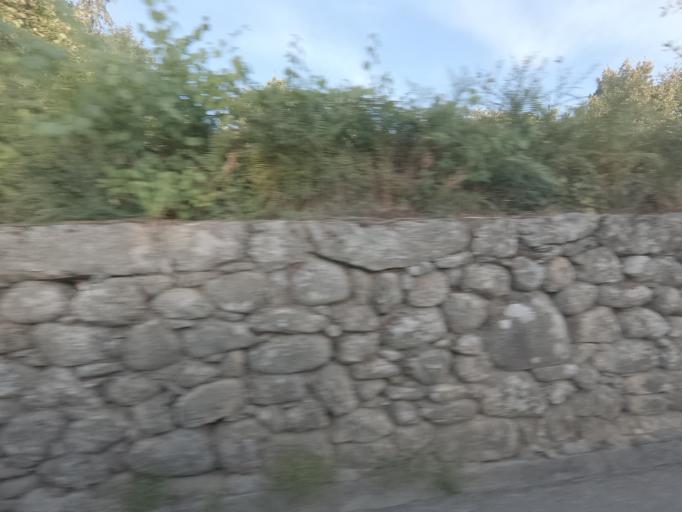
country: PT
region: Vila Real
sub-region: Vila Real
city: Vila Real
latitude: 41.3132
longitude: -7.7646
